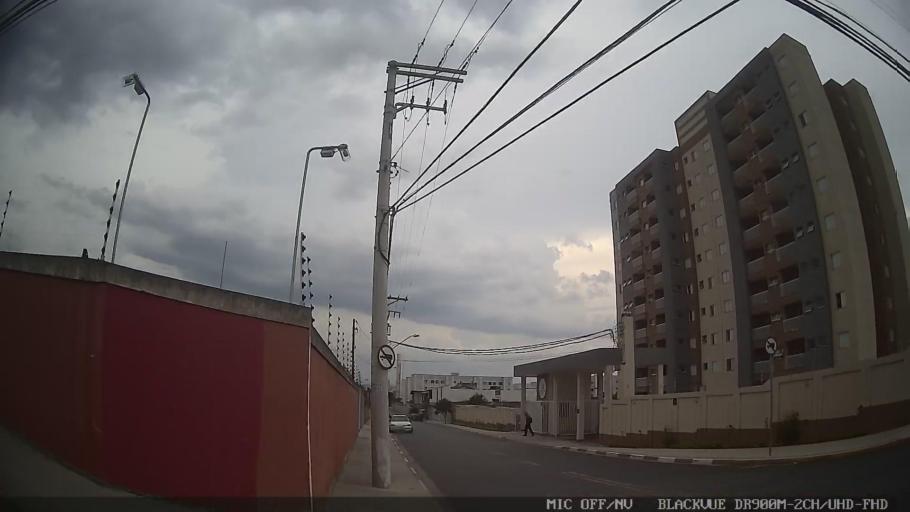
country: BR
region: Sao Paulo
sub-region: Suzano
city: Suzano
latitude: -23.5476
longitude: -46.2888
